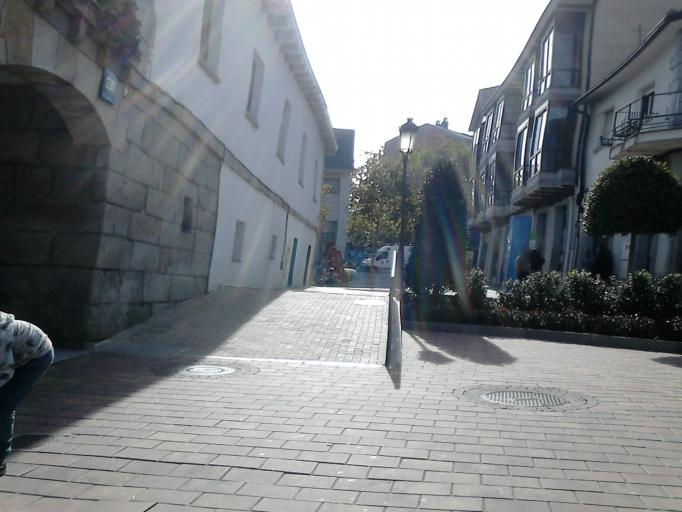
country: ES
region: Madrid
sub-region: Provincia de Madrid
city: Galapagar
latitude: 40.5773
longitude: -4.0038
